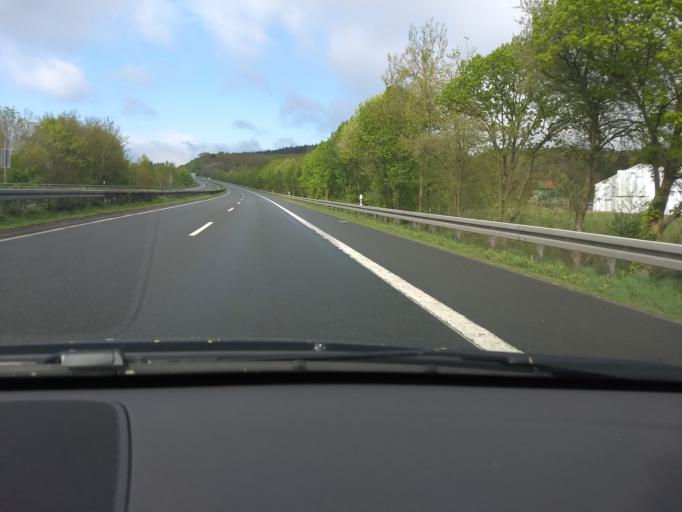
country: DE
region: North Rhine-Westphalia
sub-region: Regierungsbezirk Arnsberg
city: Meschede
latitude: 51.3597
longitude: 8.2423
